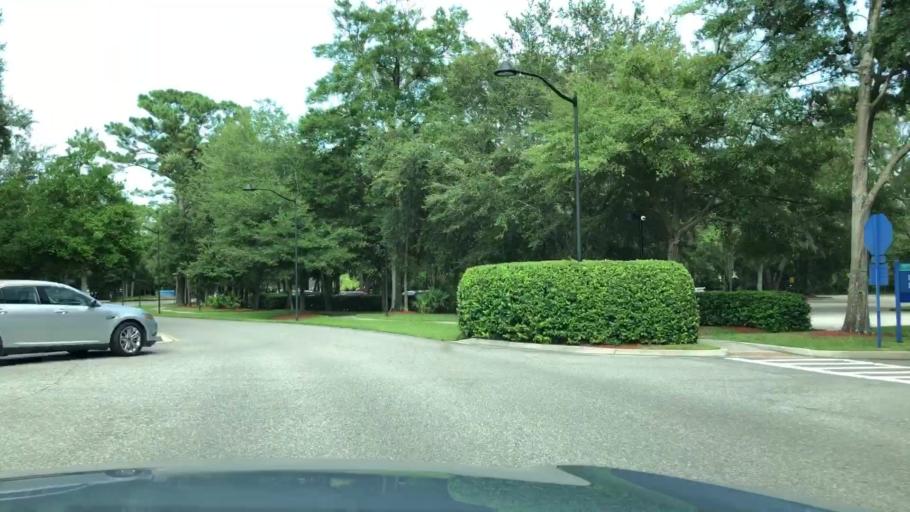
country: US
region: Florida
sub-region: Duval County
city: Jacksonville Beach
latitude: 30.2617
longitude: -81.4397
